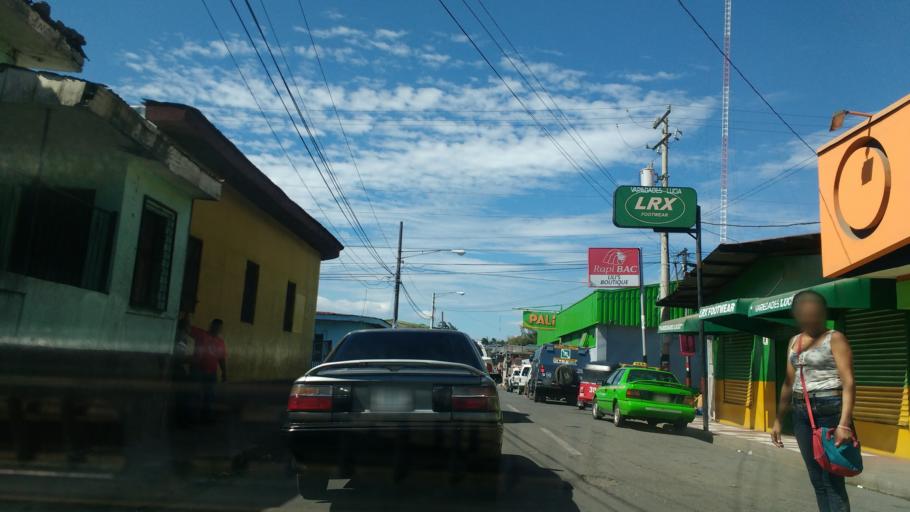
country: NI
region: Carazo
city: Diriamba
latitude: 11.8594
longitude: -86.2370
